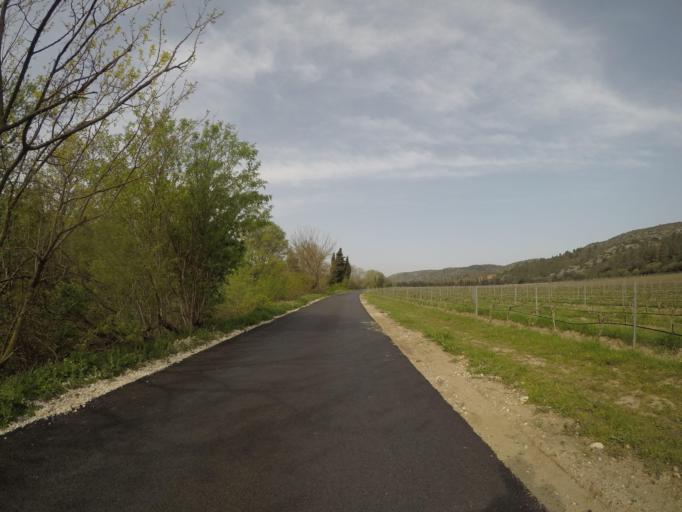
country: FR
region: Languedoc-Roussillon
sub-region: Departement des Pyrenees-Orientales
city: Estagel
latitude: 42.7753
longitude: 2.7461
